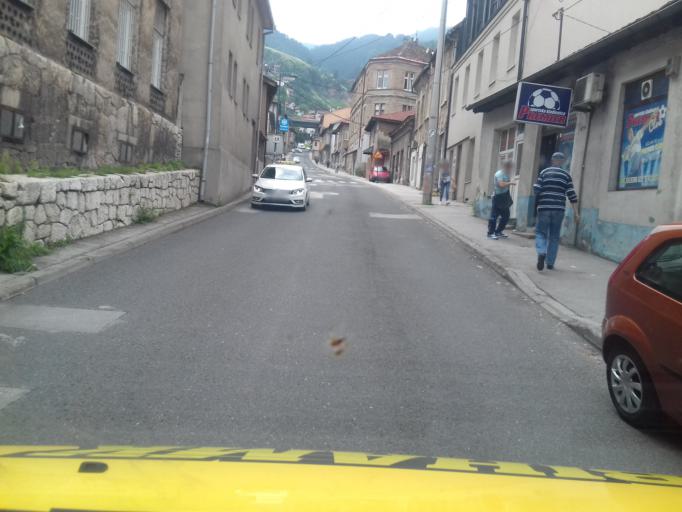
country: BA
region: Federation of Bosnia and Herzegovina
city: Kobilja Glava
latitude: 43.8546
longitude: 18.4301
